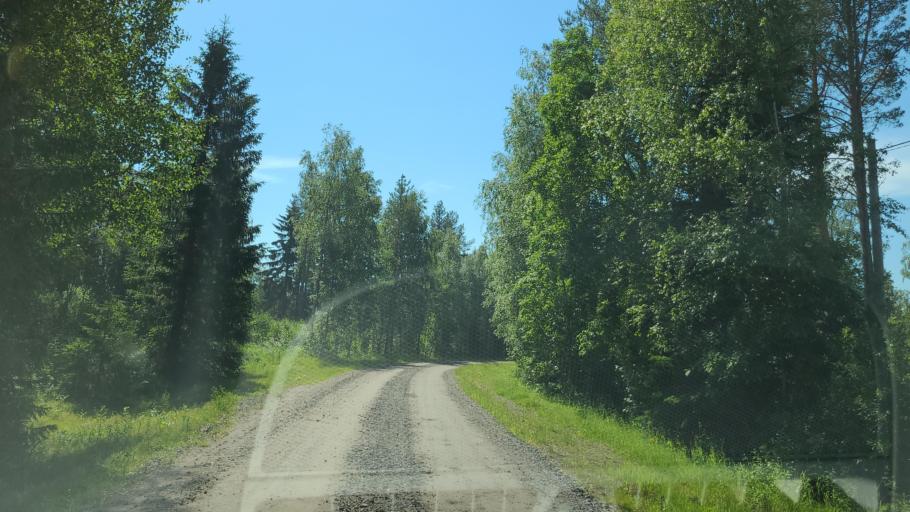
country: SE
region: Vaesterbotten
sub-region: Robertsfors Kommun
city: Robertsfors
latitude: 64.0899
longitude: 20.8493
